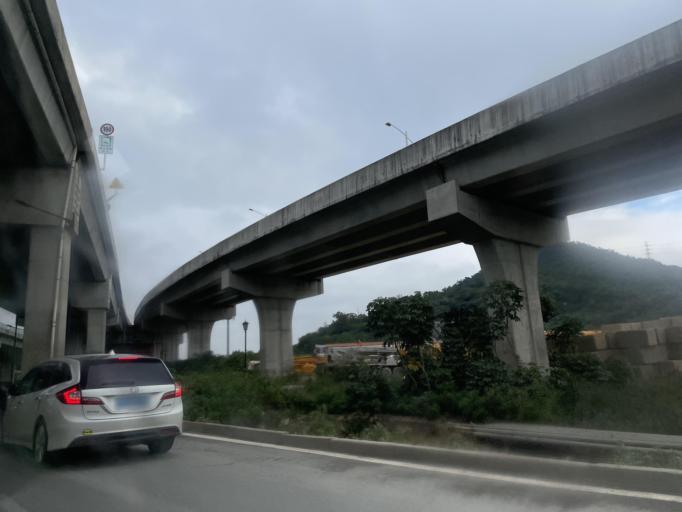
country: CN
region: Guangdong
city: Nanping
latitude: 22.1781
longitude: 113.4634
